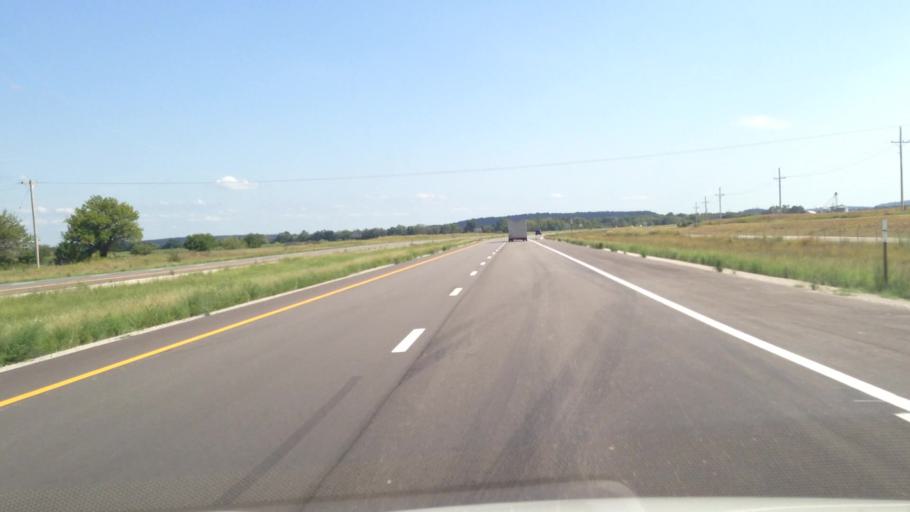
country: US
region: Kansas
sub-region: Linn County
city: La Cygne
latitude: 38.3389
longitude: -94.6799
